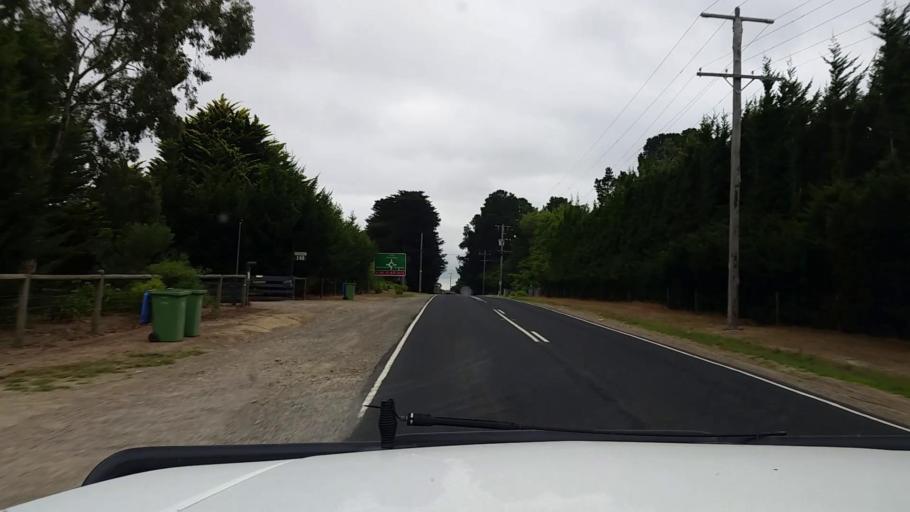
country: AU
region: Victoria
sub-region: Mornington Peninsula
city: Hastings
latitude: -38.2877
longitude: 145.1456
